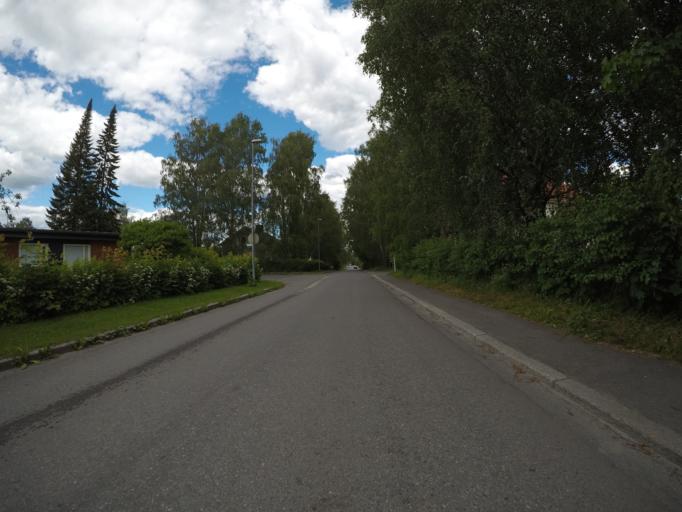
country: FI
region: Haeme
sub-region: Haemeenlinna
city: Haemeenlinna
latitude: 60.9955
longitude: 24.4357
